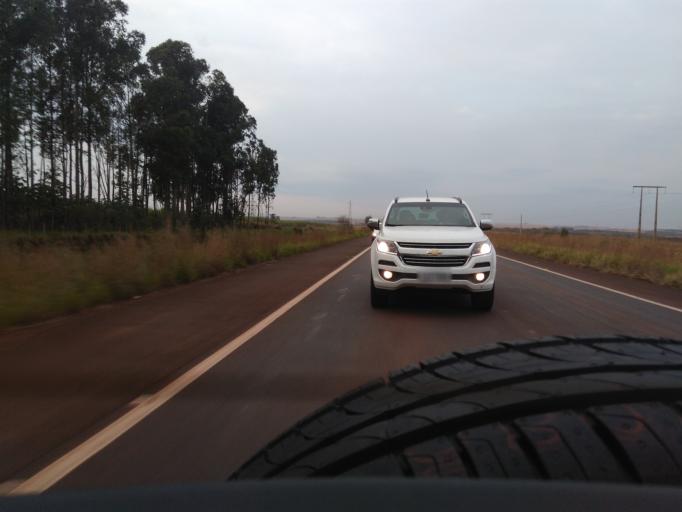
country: BR
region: Mato Grosso do Sul
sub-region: Dourados
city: Dourados
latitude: -22.2999
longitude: -55.0921
